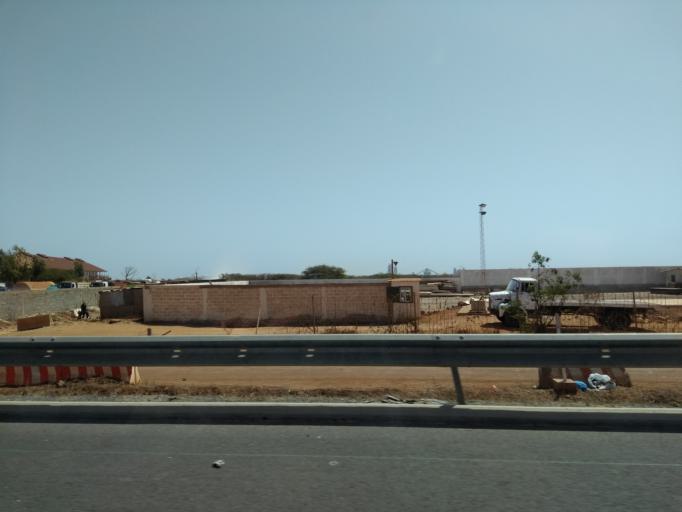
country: SN
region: Dakar
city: Pikine
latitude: 14.7320
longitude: -17.2395
